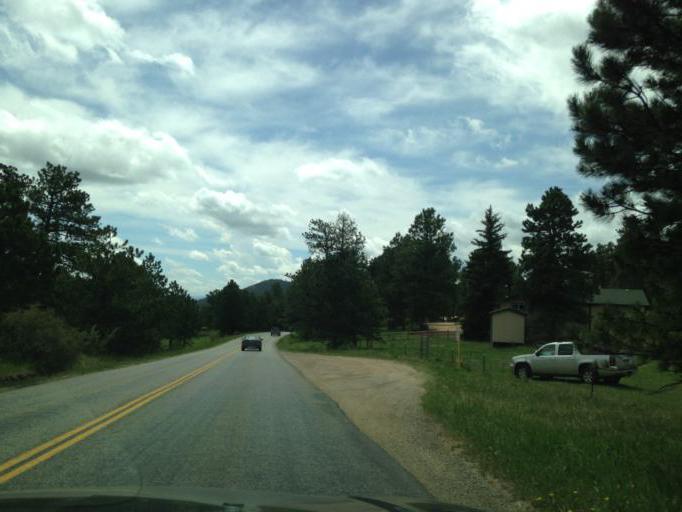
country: US
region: Colorado
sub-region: Jefferson County
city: Evergreen
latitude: 39.4467
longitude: -105.4633
